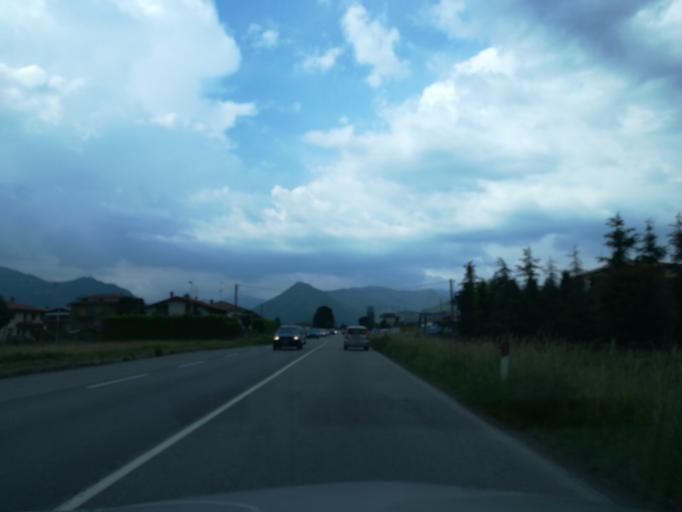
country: IT
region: Lombardy
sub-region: Provincia di Bergamo
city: Scano al Brembo
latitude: 45.7216
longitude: 9.6100
